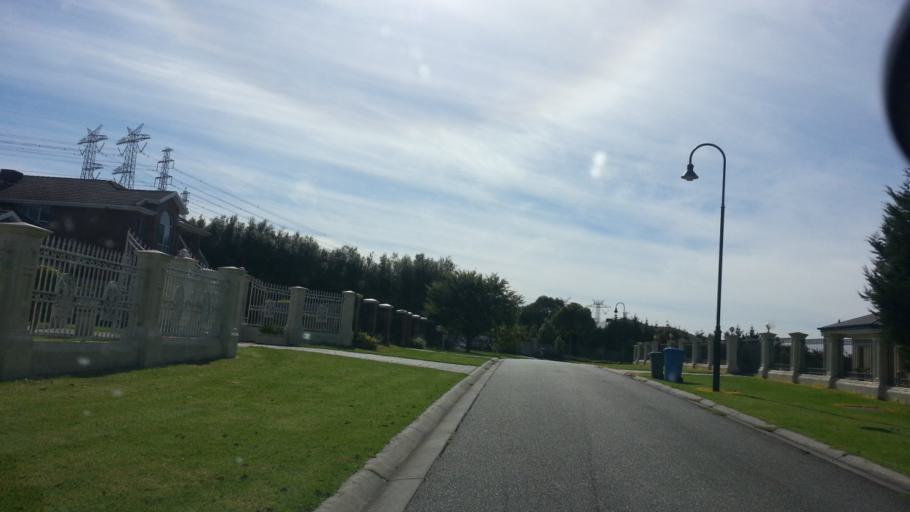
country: AU
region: Victoria
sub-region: Casey
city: Endeavour Hills
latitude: -37.9746
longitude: 145.2851
